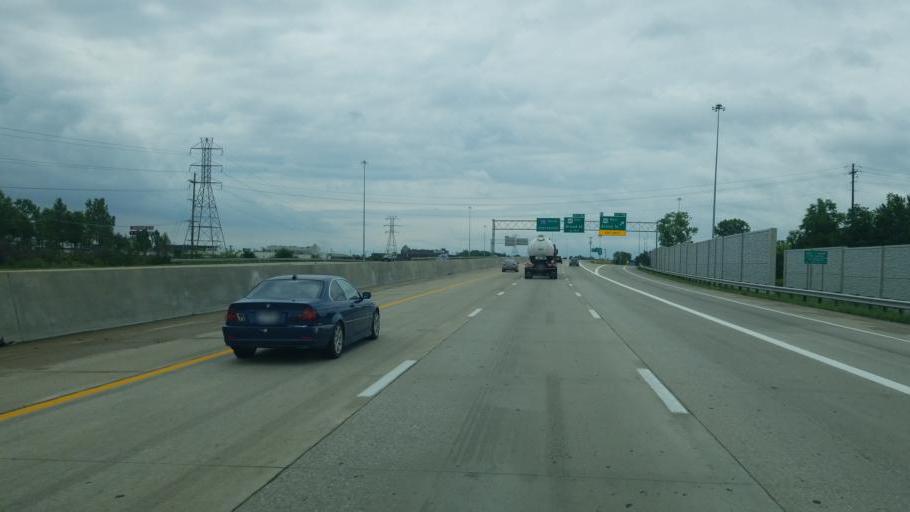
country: US
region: Ohio
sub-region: Franklin County
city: Lincoln Village
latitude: 39.9572
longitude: -83.1192
